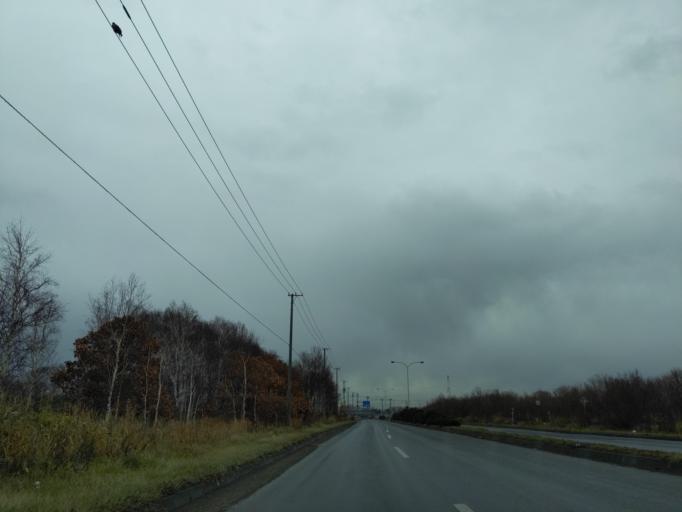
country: JP
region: Hokkaido
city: Ishikari
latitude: 43.1884
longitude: 141.3028
